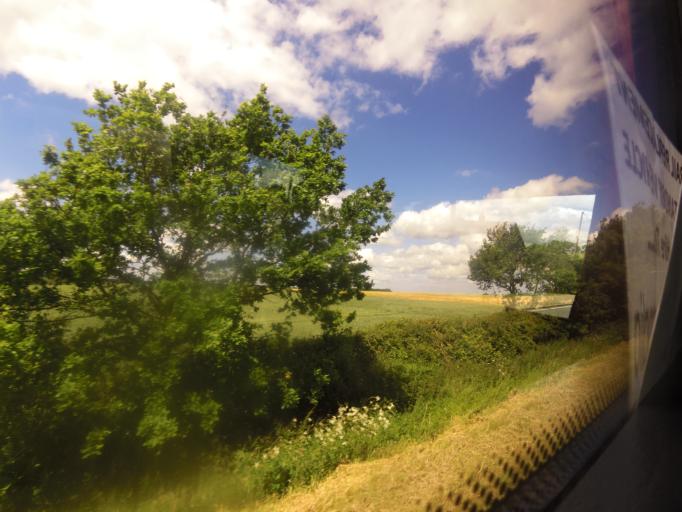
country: GB
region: England
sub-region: Norfolk
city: Aylsham
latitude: 52.7793
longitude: 1.2552
